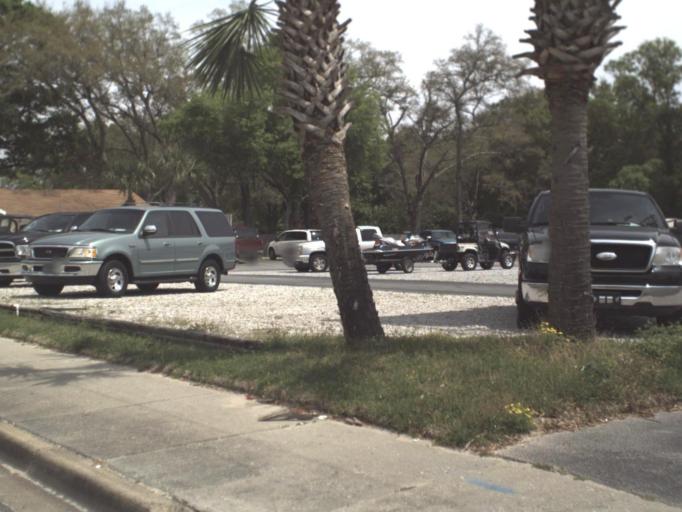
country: US
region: Florida
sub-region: Okaloosa County
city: Wright
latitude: 30.4578
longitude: -86.6361
